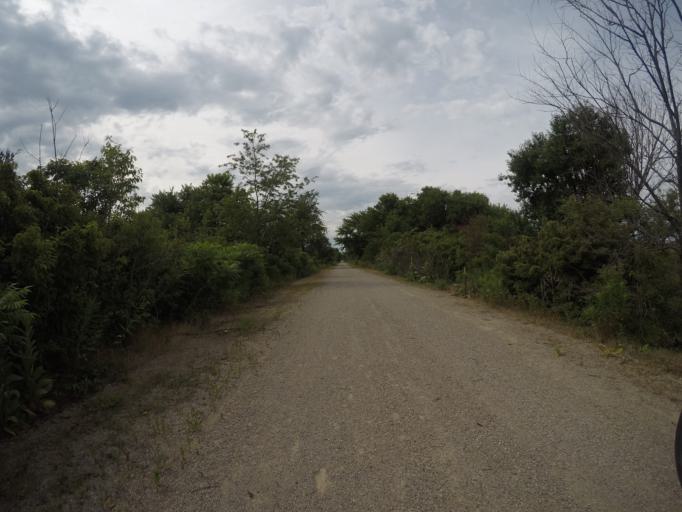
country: US
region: Kansas
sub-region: Anderson County
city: Garnett
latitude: 38.4298
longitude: -95.2635
